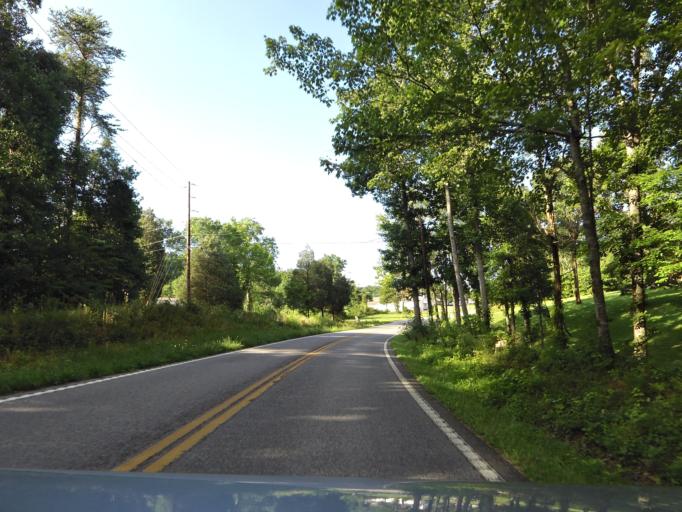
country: US
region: Tennessee
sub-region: Blount County
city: Maryville
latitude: 35.6275
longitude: -84.0240
